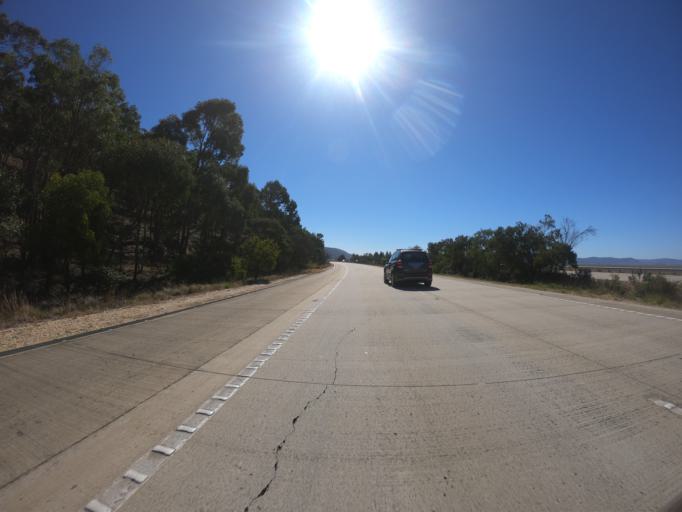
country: AU
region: New South Wales
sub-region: Yass Valley
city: Gundaroo
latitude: -35.0954
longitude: 149.3761
